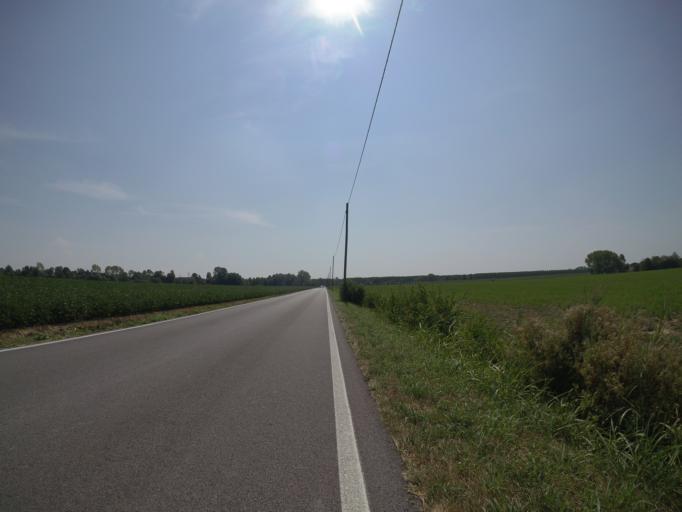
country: IT
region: Friuli Venezia Giulia
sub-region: Provincia di Udine
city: Pocenia
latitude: 45.8517
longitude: 13.0920
